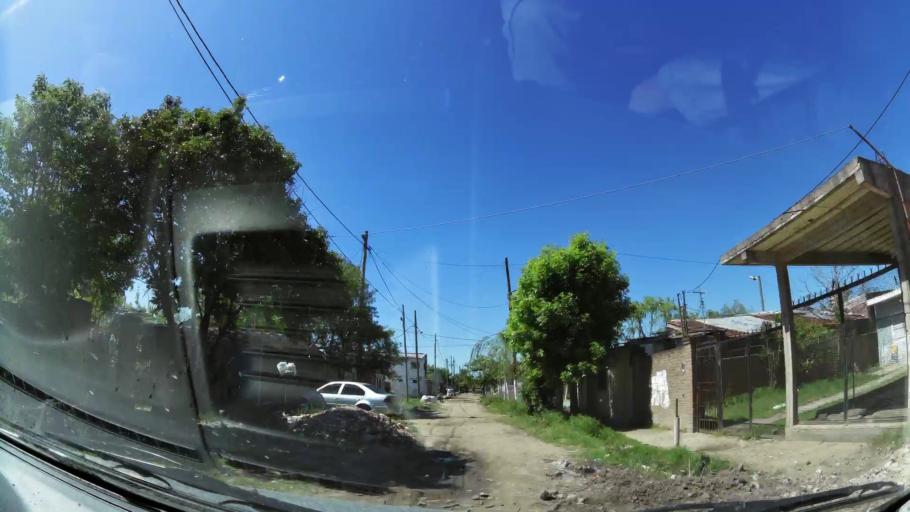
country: AR
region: Buenos Aires
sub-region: Partido de Quilmes
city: Quilmes
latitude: -34.7286
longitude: -58.3128
